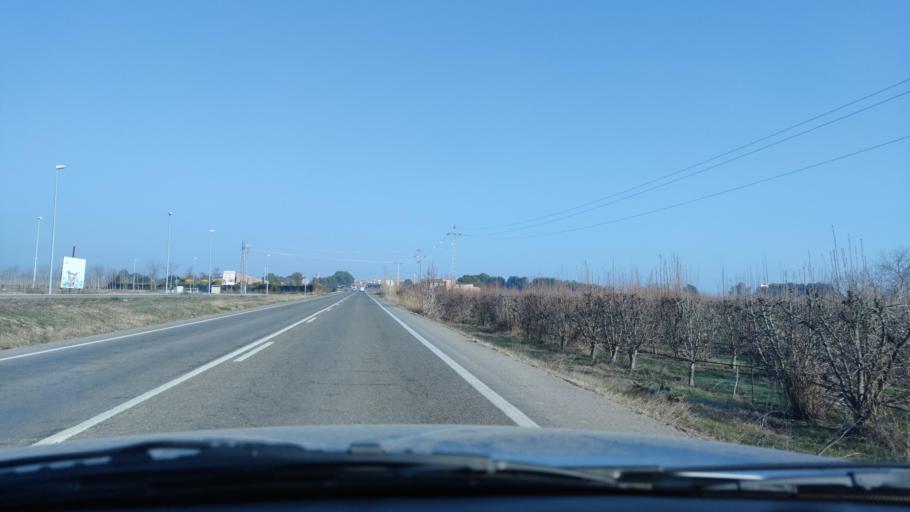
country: ES
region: Catalonia
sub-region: Provincia de Lleida
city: Torrefarrera
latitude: 41.6820
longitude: 0.6321
